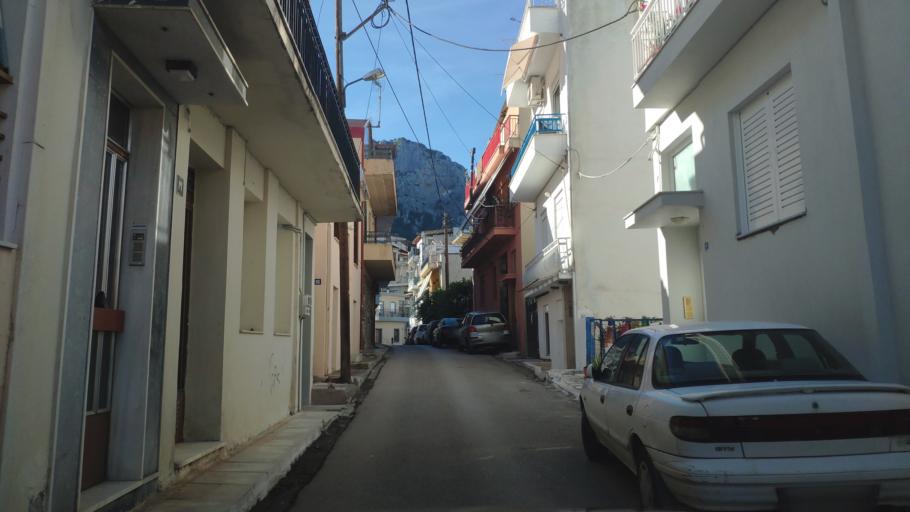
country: GR
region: Central Greece
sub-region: Nomos Voiotias
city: Livadeia
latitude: 38.4345
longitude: 22.8763
